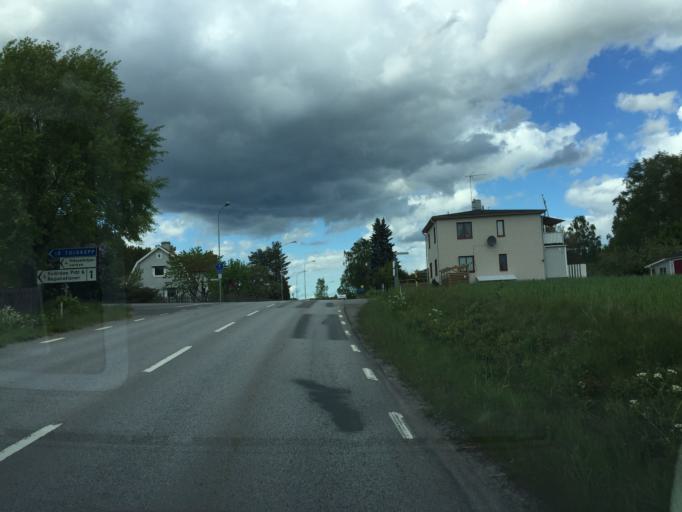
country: SE
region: OEstergoetland
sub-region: Finspangs Kommun
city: Finspang
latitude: 58.6782
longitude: 15.7516
